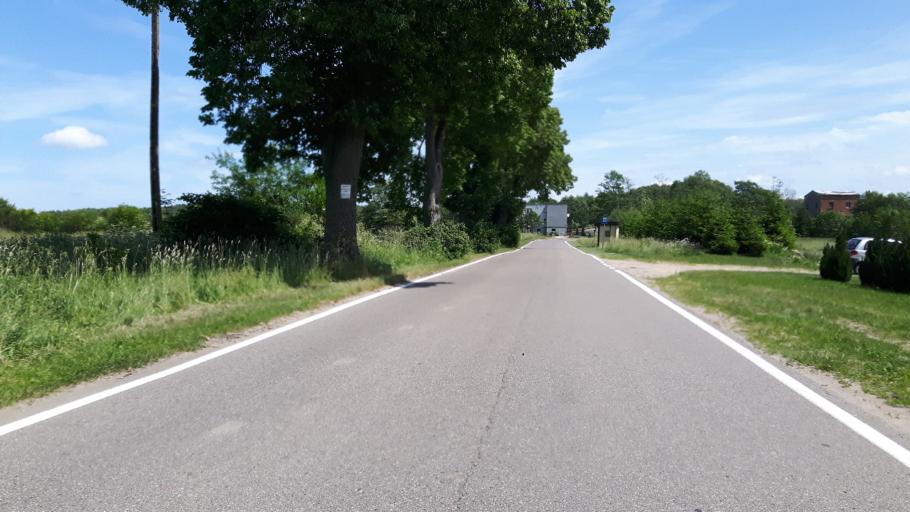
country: PL
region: Pomeranian Voivodeship
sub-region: Powiat wejherowski
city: Gniewino
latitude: 54.7247
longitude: 17.9752
